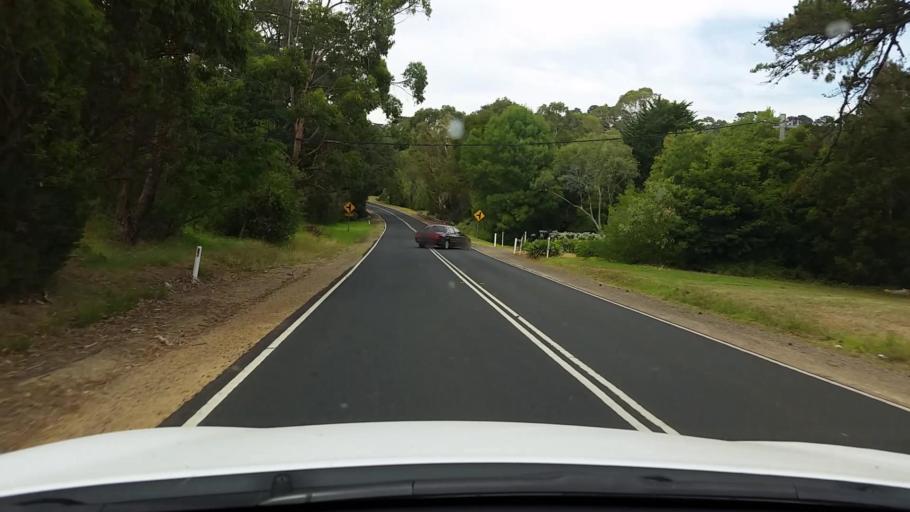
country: AU
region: Victoria
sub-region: Mornington Peninsula
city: Merricks
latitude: -38.4277
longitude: 145.0424
